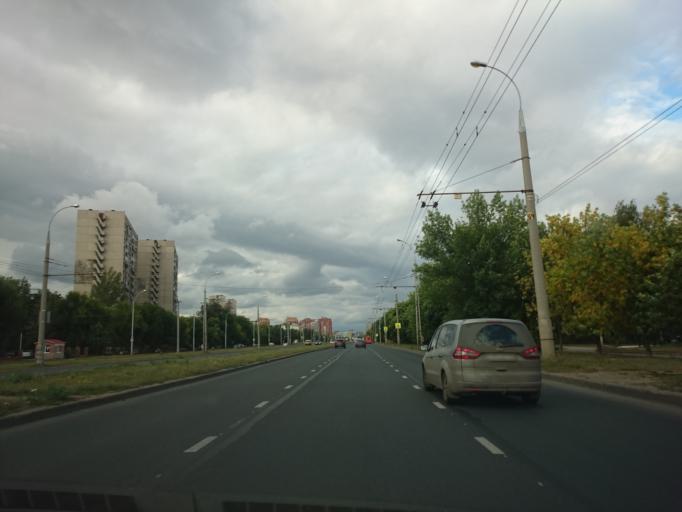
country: RU
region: Samara
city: Tol'yatti
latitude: 53.5067
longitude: 49.3016
